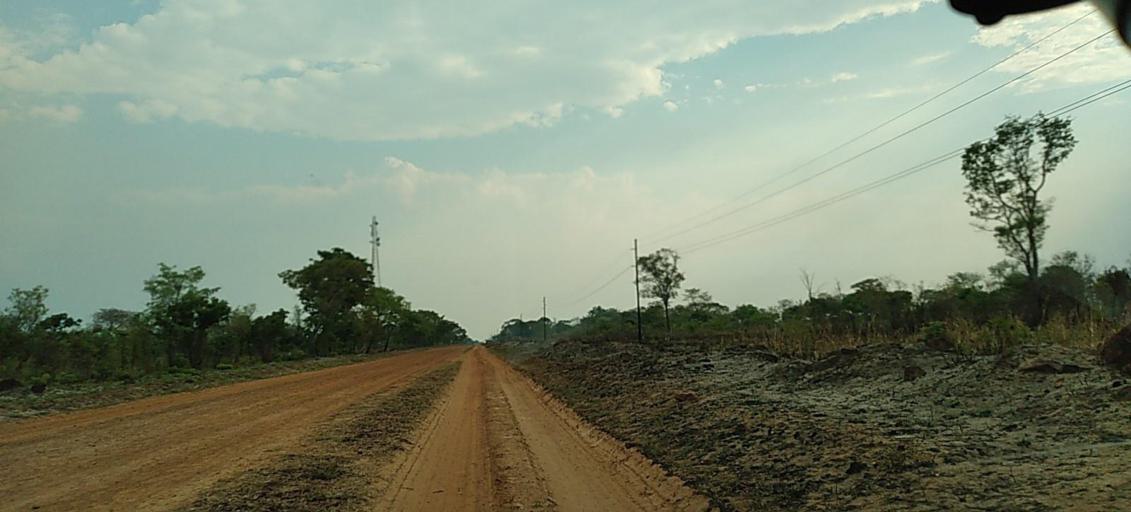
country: ZM
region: North-Western
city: Kabompo
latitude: -13.8821
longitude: 23.6633
